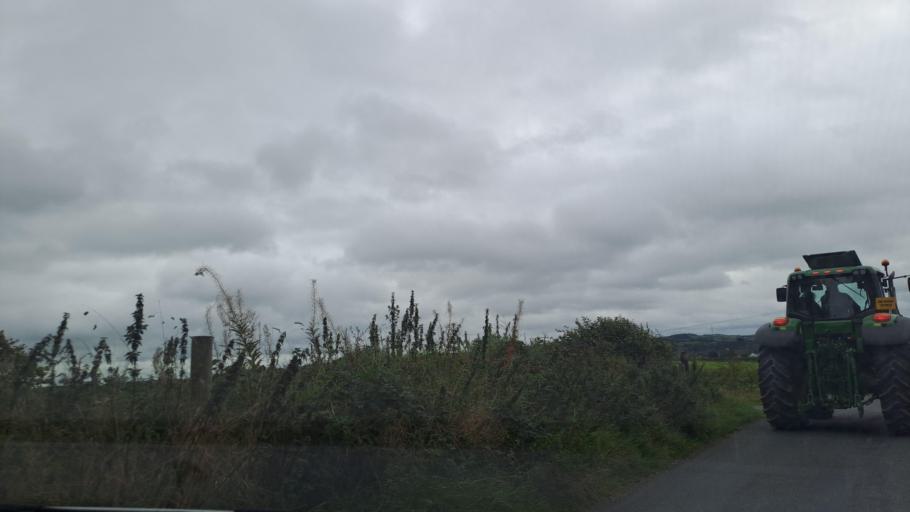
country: IE
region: Ulster
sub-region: An Cabhan
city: Bailieborough
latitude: 54.0052
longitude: -6.8915
